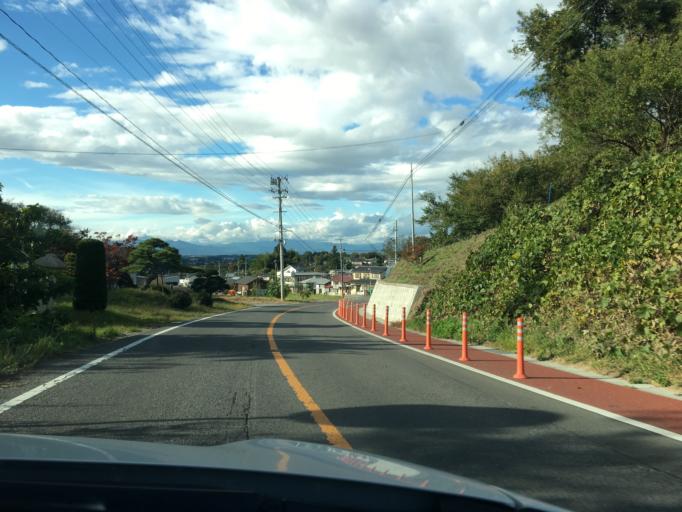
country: JP
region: Fukushima
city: Sukagawa
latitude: 37.2618
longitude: 140.4227
